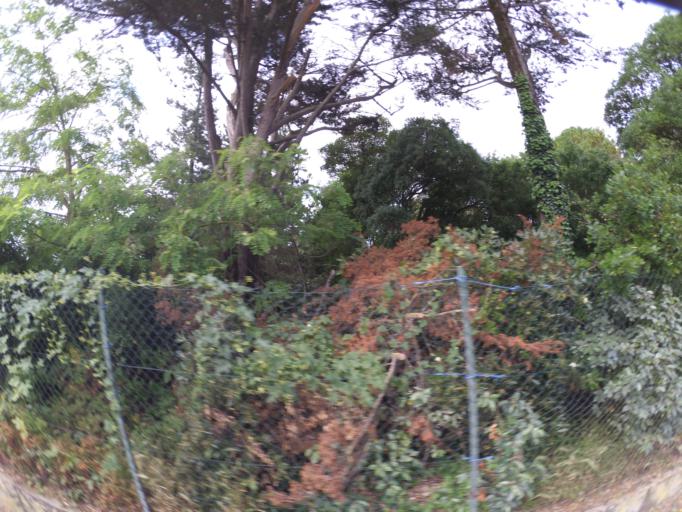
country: FR
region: Poitou-Charentes
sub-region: Departement de la Charente-Maritime
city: Angoulins
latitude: 46.0955
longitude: -1.1020
